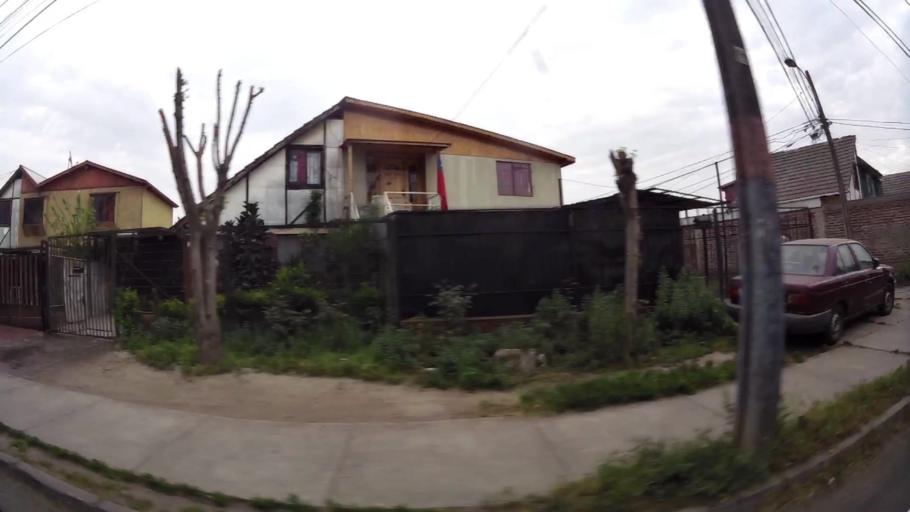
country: CL
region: Santiago Metropolitan
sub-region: Provincia de Santiago
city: Lo Prado
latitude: -33.4817
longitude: -70.7279
